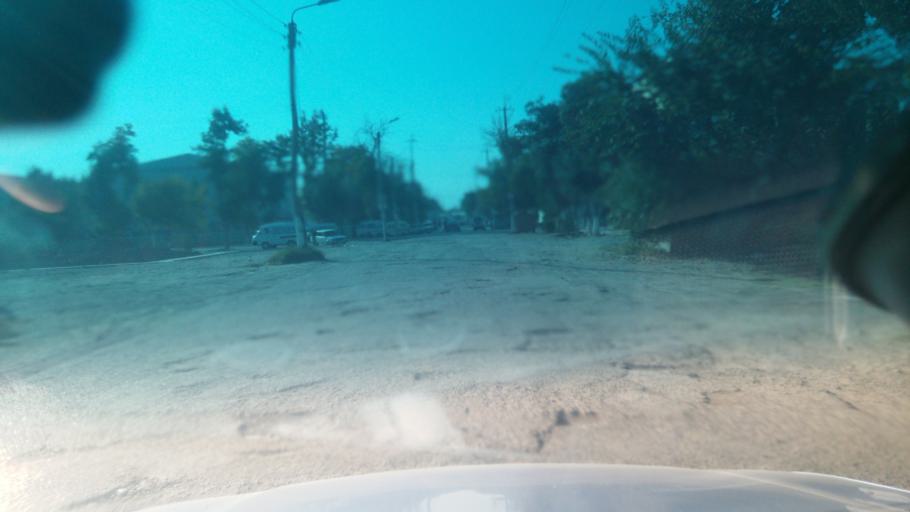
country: UZ
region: Sirdaryo
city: Guliston
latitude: 40.4969
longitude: 68.7689
